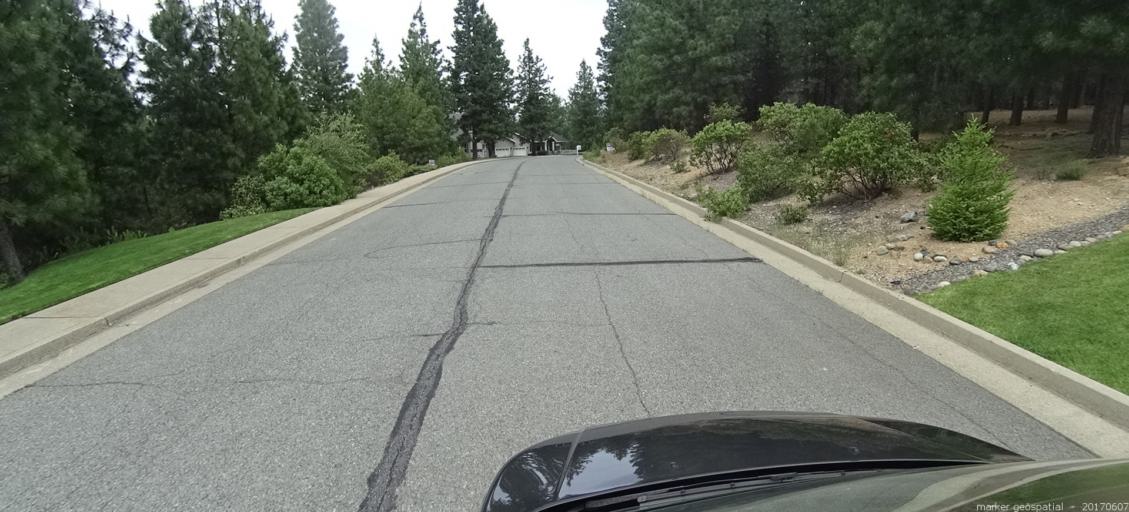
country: US
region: California
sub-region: Siskiyou County
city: Mount Shasta
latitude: 41.2895
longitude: -122.3160
